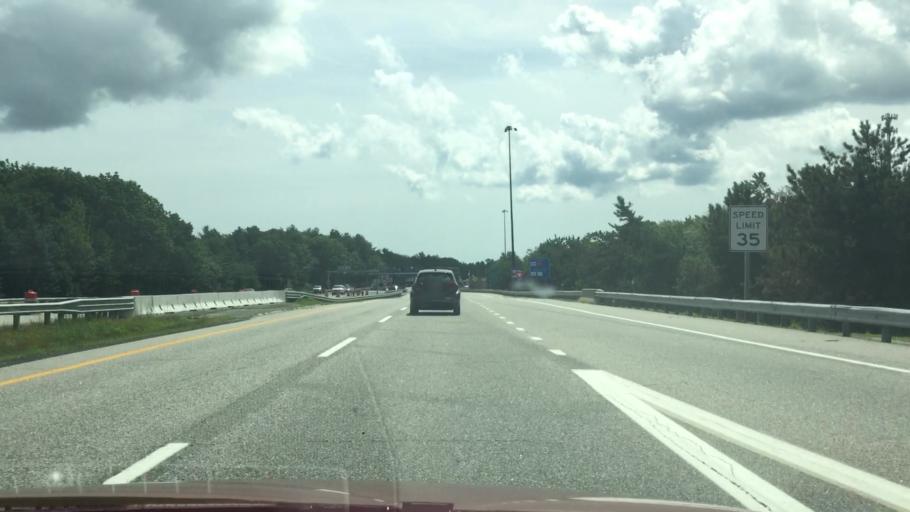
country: US
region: Maine
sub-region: York County
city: Saco
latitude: 43.5257
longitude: -70.4497
